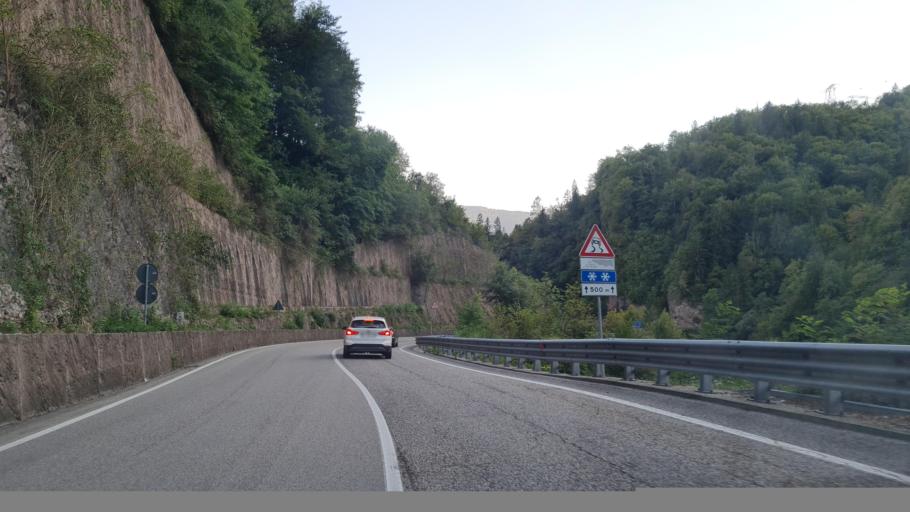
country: IT
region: Veneto
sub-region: Provincia di Belluno
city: Lamon
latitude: 46.0628
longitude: 11.7639
